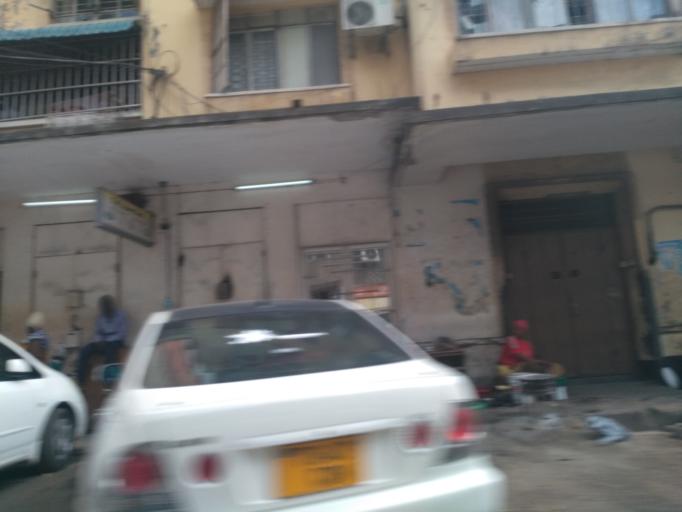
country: TZ
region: Dar es Salaam
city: Dar es Salaam
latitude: -6.8180
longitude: 39.2815
